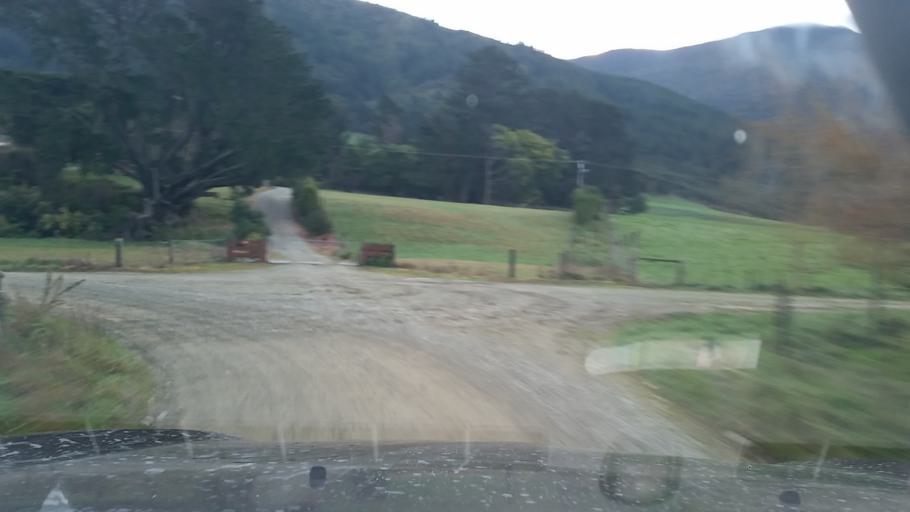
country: NZ
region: Marlborough
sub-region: Marlborough District
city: Picton
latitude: -41.1430
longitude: 174.1358
